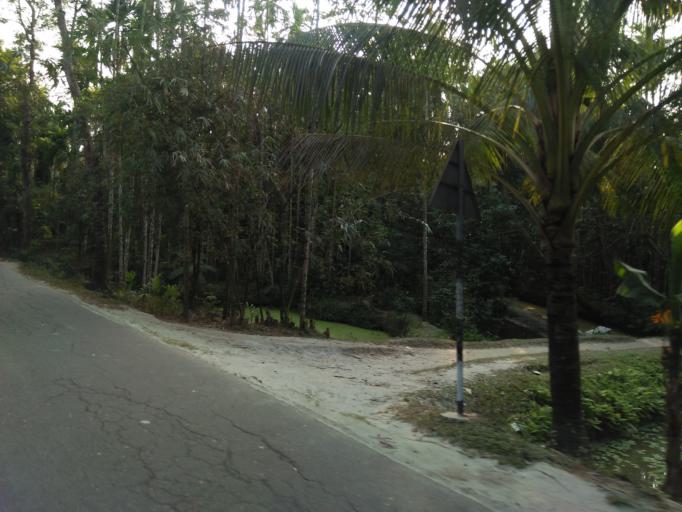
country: BD
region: Barisal
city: Bhola
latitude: 22.7094
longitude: 90.6402
